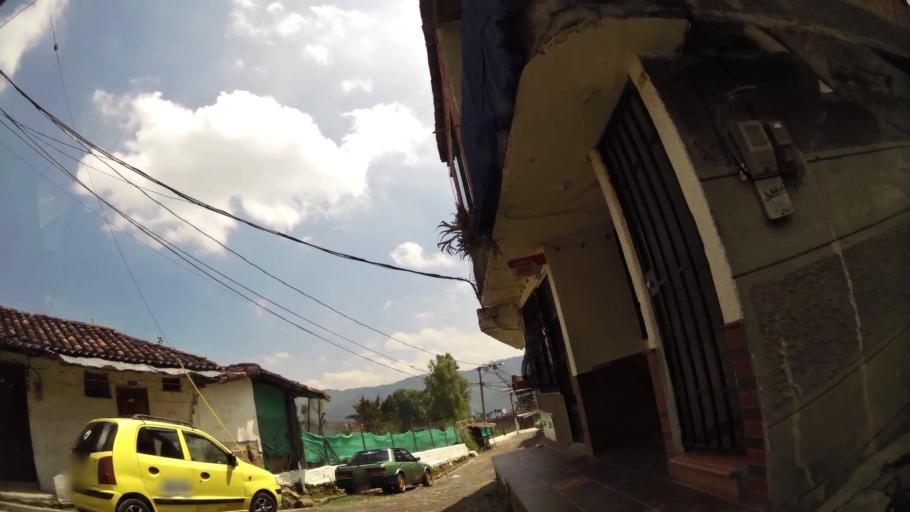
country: CO
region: Antioquia
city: La Estrella
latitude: 6.1809
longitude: -75.6612
